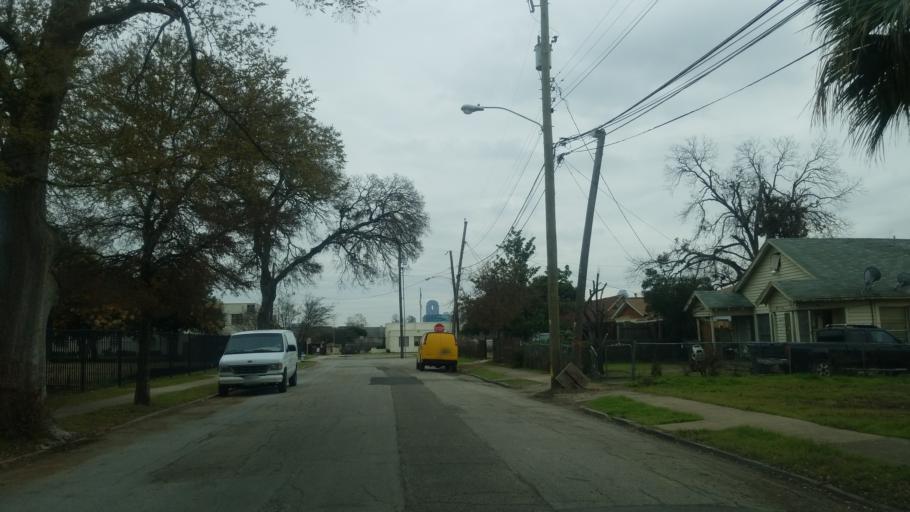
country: US
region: Texas
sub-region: Dallas County
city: Dallas
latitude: 32.8140
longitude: -96.8234
